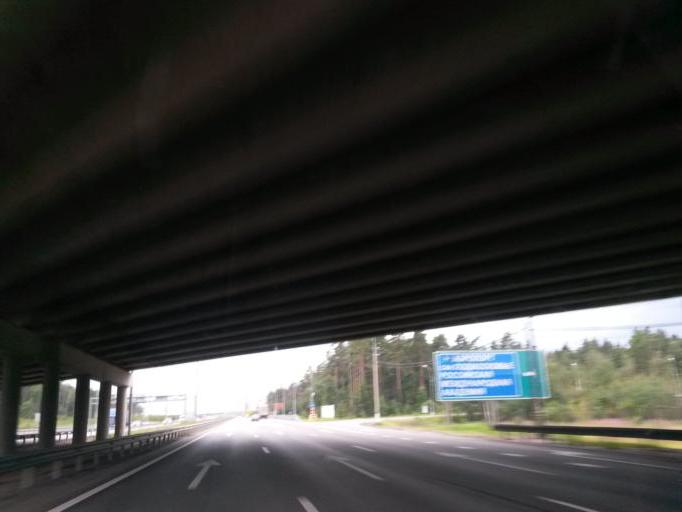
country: RU
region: Moskovskaya
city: Vostryakovo
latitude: 55.4054
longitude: 37.7851
